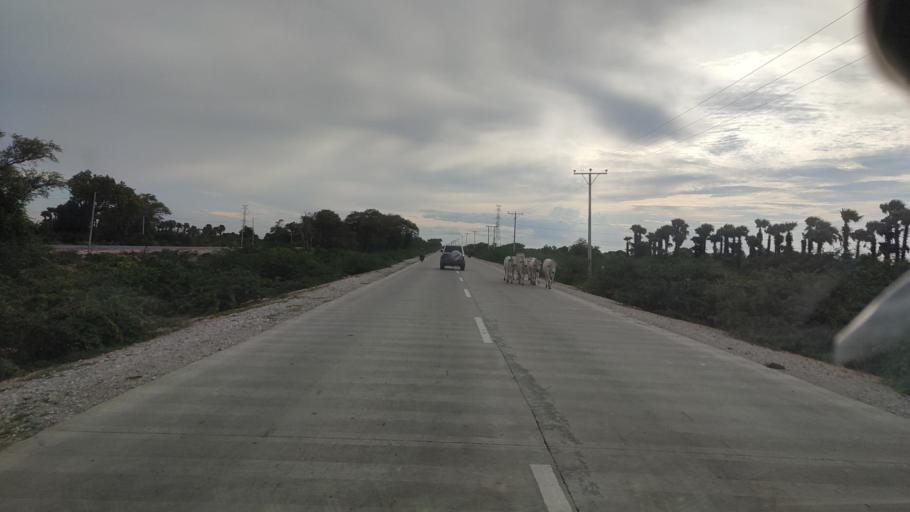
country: MM
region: Mandalay
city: Kyaukse
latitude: 21.3465
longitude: 96.0994
